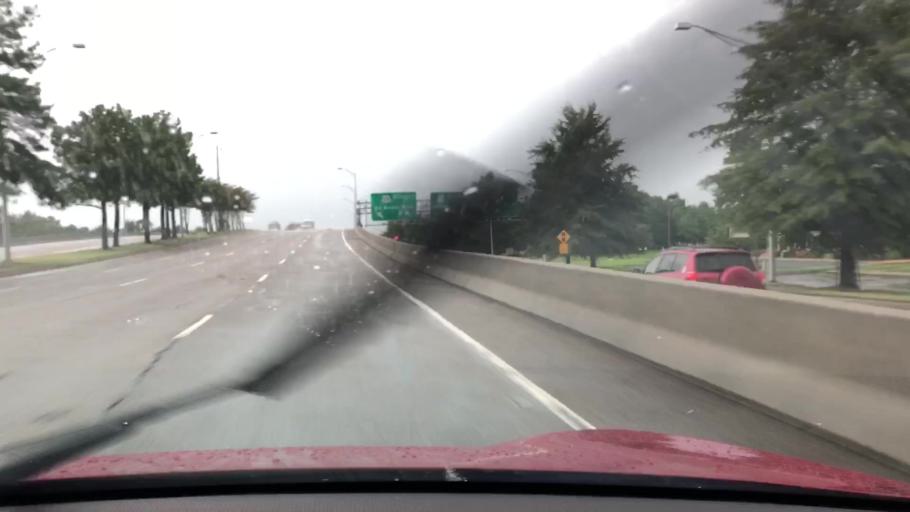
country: US
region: Virginia
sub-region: City of Chesapeake
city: Chesapeake
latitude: 36.8539
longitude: -76.2098
